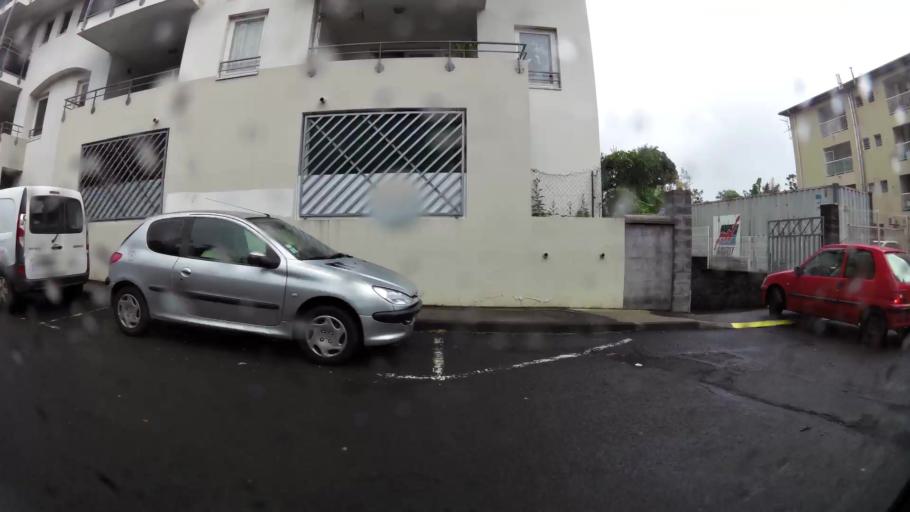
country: RE
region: Reunion
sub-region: Reunion
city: Saint-Andre
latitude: -20.9602
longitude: 55.6527
